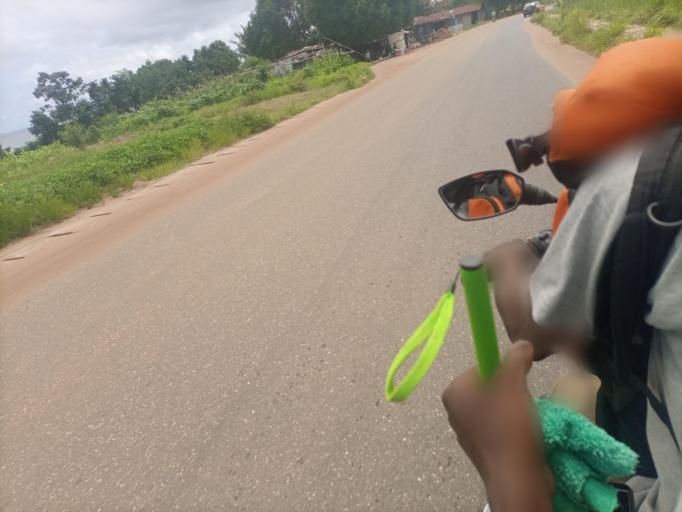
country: SL
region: Northern Province
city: Tintafor
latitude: 8.6220
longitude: -13.2132
